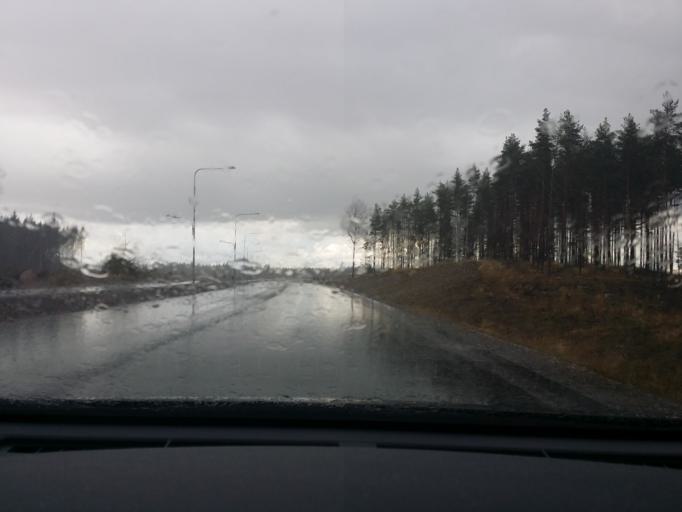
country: SE
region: Soedermanland
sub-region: Eskilstuna Kommun
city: Arla
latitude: 59.3601
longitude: 16.7003
